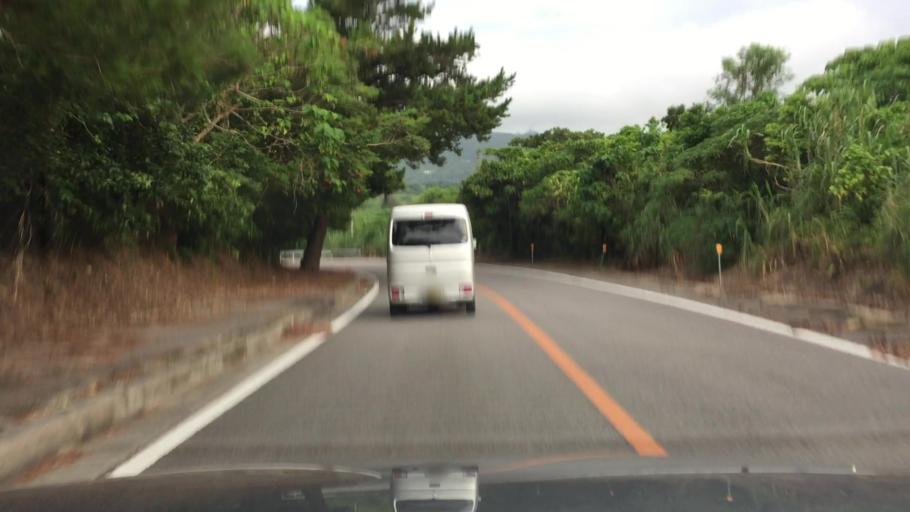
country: JP
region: Okinawa
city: Ishigaki
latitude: 24.4044
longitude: 124.1470
